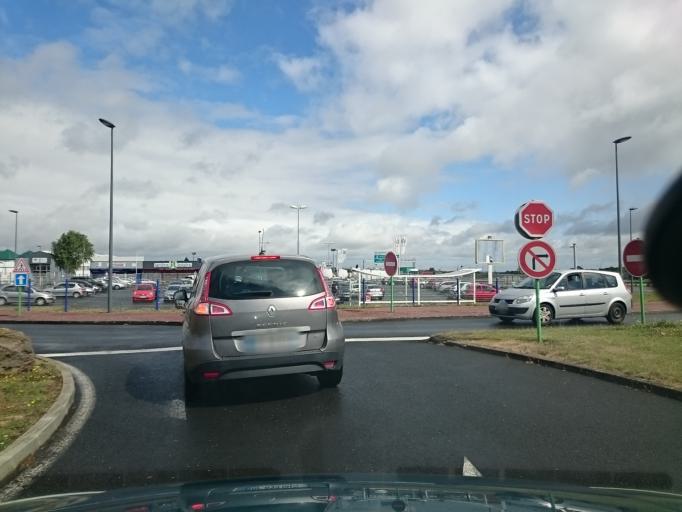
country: FR
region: Lower Normandy
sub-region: Departement du Calvados
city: Ifs
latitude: 49.1423
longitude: -0.3379
